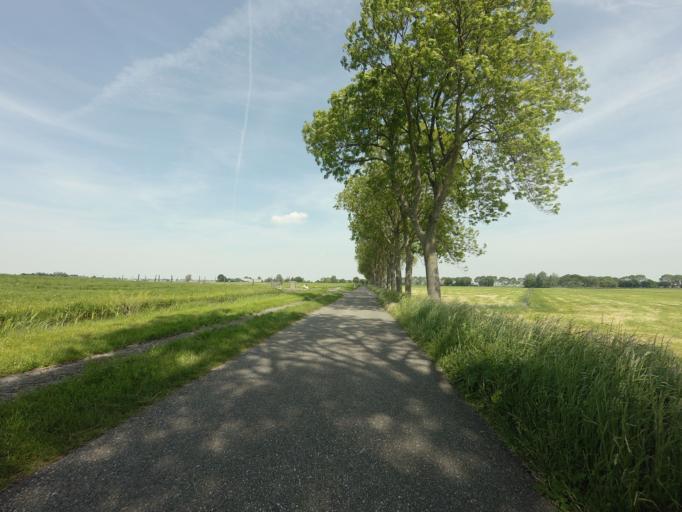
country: NL
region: Utrecht
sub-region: Gemeente De Ronde Venen
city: Mijdrecht
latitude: 52.2303
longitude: 4.8834
